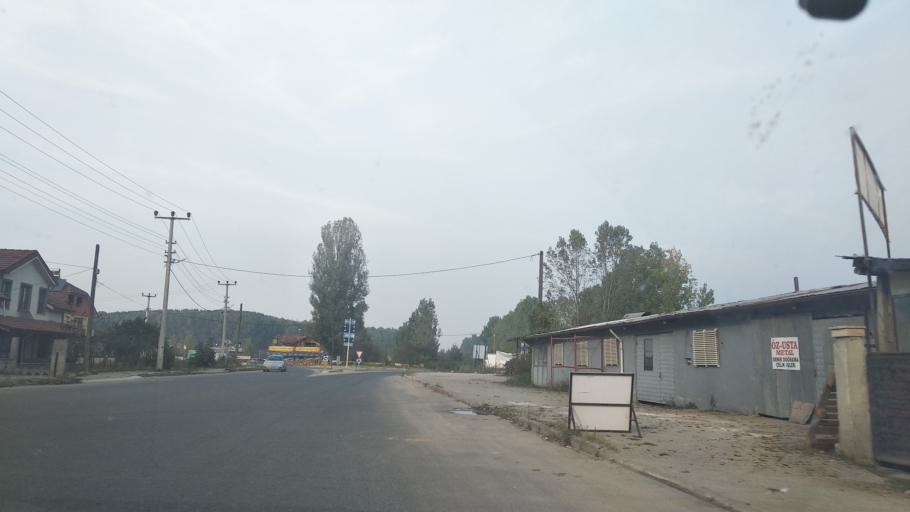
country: TR
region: Duzce
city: Duzce
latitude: 40.8198
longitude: 31.1772
